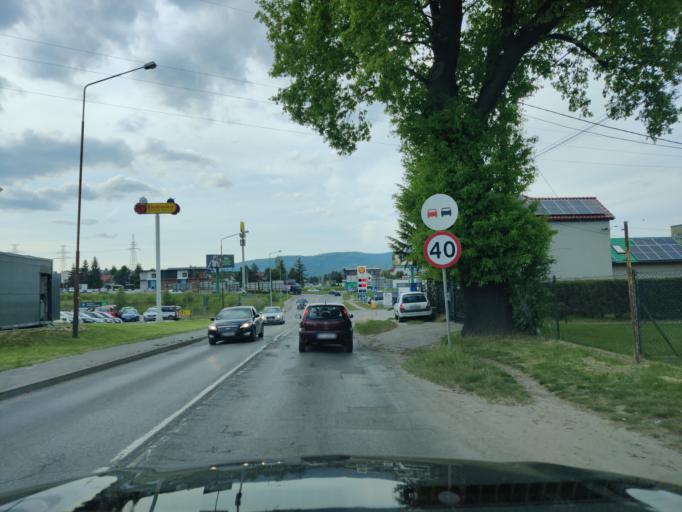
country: PL
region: Silesian Voivodeship
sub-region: Powiat zywiecki
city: Zywiec
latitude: 49.6892
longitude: 19.1828
